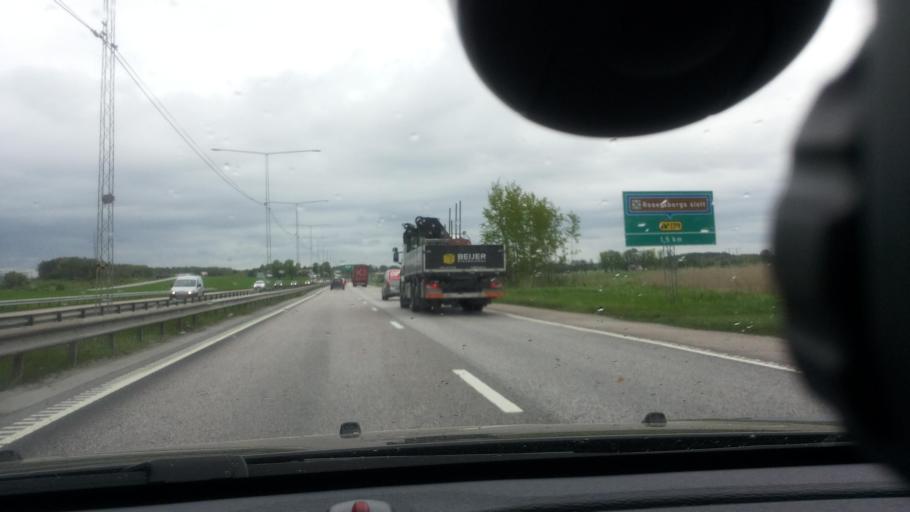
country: SE
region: Stockholm
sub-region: Sigtuna Kommun
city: Rosersberg
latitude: 59.5594
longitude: 17.8980
